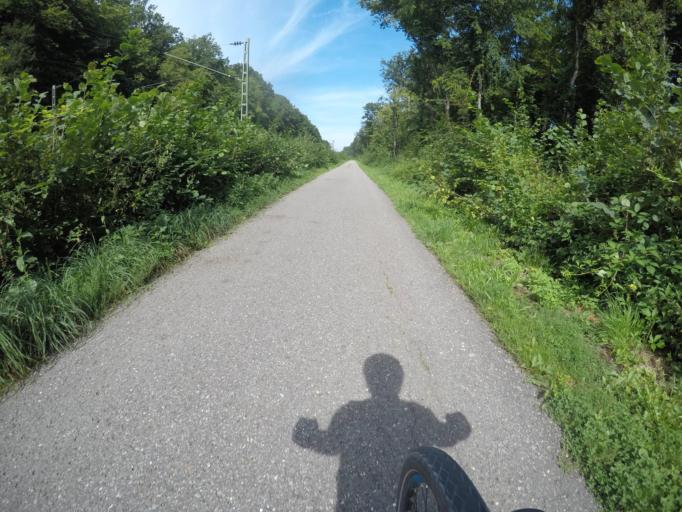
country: DE
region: Baden-Wuerttemberg
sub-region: Karlsruhe Region
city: Otisheim
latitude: 48.9744
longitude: 8.7976
